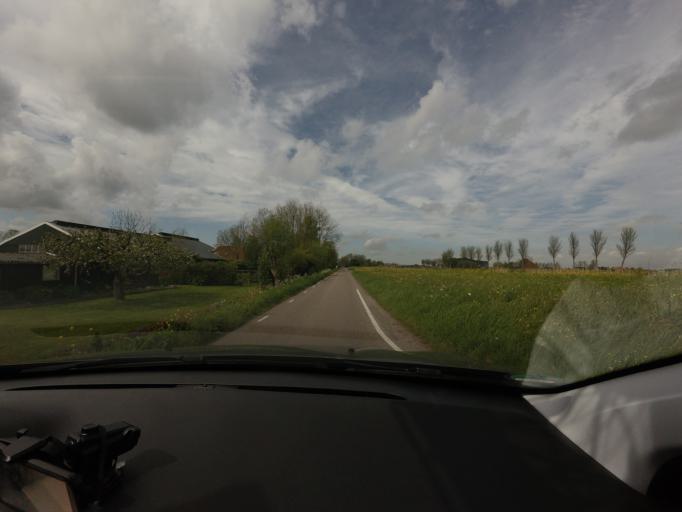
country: NL
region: North Holland
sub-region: Gemeente Beemster
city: Halfweg
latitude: 52.5194
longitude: 4.8772
